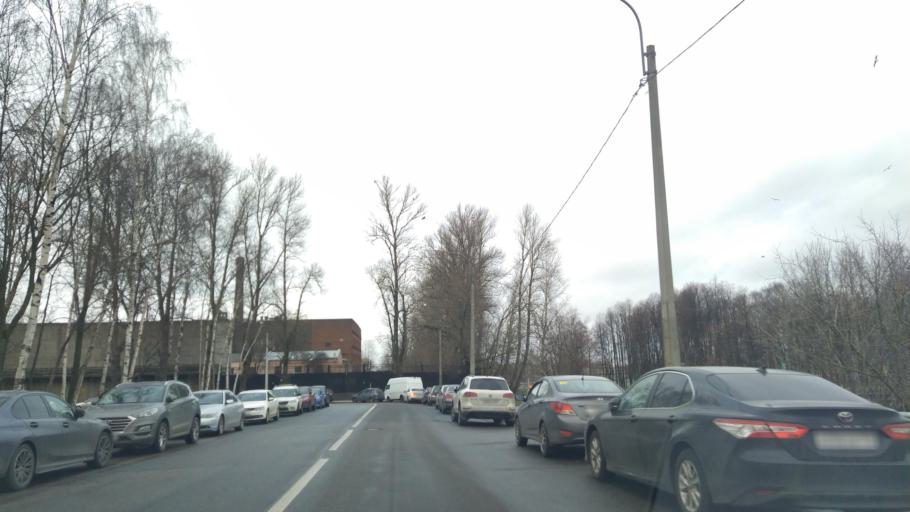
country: RU
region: St.-Petersburg
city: Centralniy
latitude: 59.9173
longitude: 30.3812
